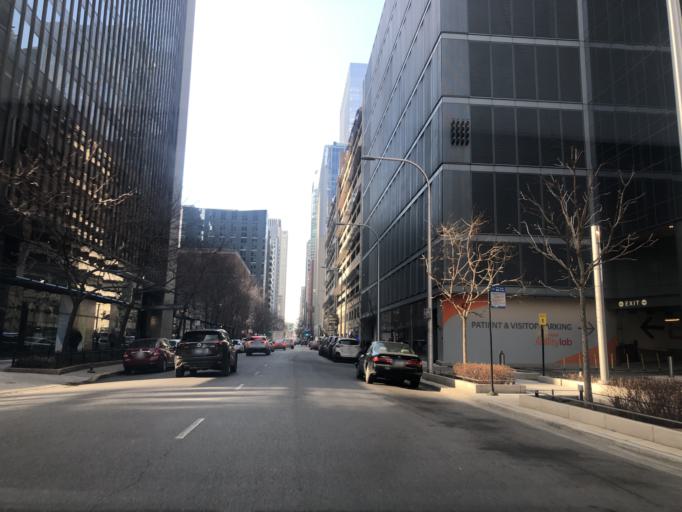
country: US
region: Illinois
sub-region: Cook County
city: Chicago
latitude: 41.8935
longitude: -87.6180
